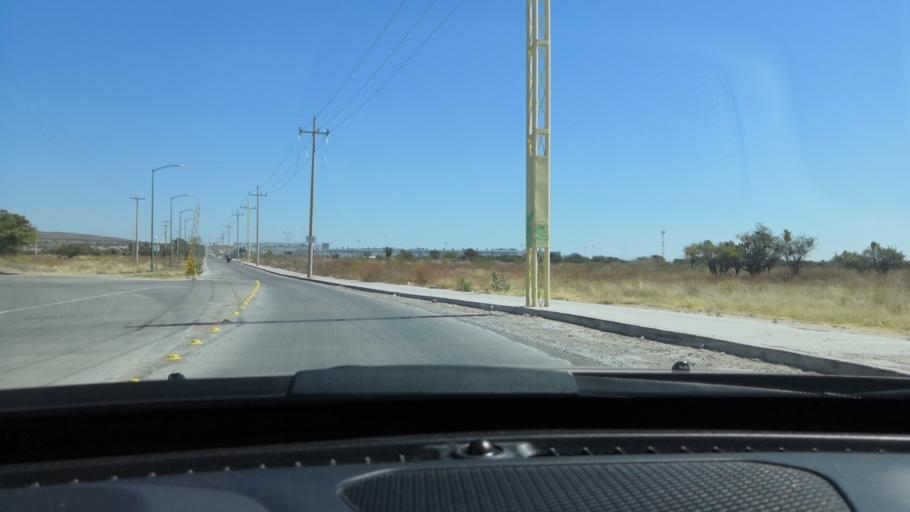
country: MX
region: Guanajuato
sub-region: Leon
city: Centro Familiar la Soledad
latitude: 21.1010
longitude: -101.7745
